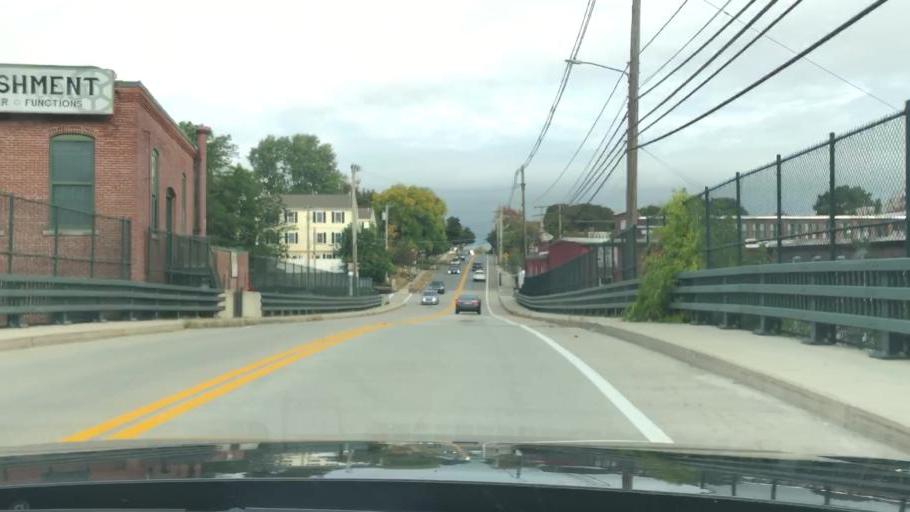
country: US
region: Massachusetts
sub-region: Middlesex County
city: Chelmsford
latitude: 42.6356
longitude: -71.3790
